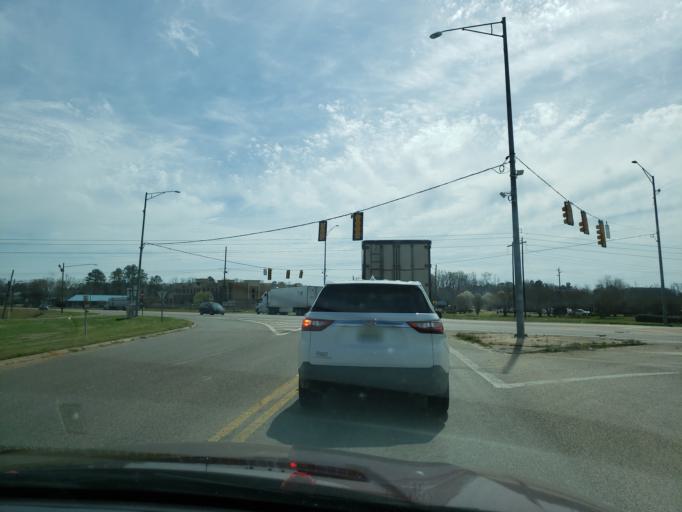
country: US
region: Alabama
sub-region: Dallas County
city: Selma
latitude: 32.4343
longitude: -87.0605
